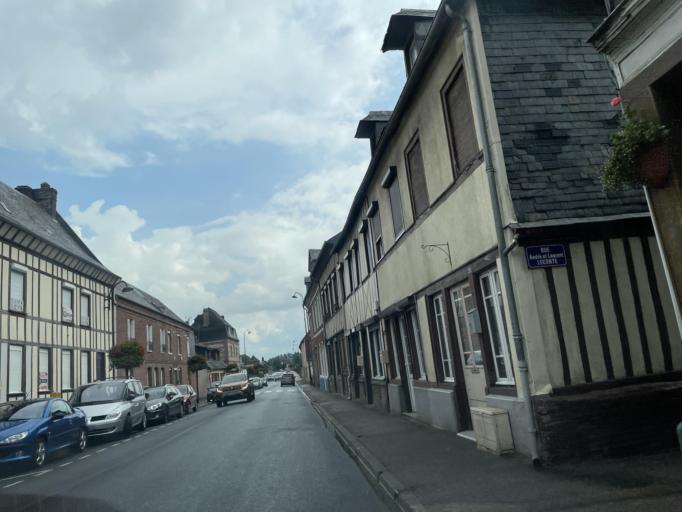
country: FR
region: Haute-Normandie
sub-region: Departement de la Seine-Maritime
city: Envermeu
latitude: 49.8949
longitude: 1.2664
